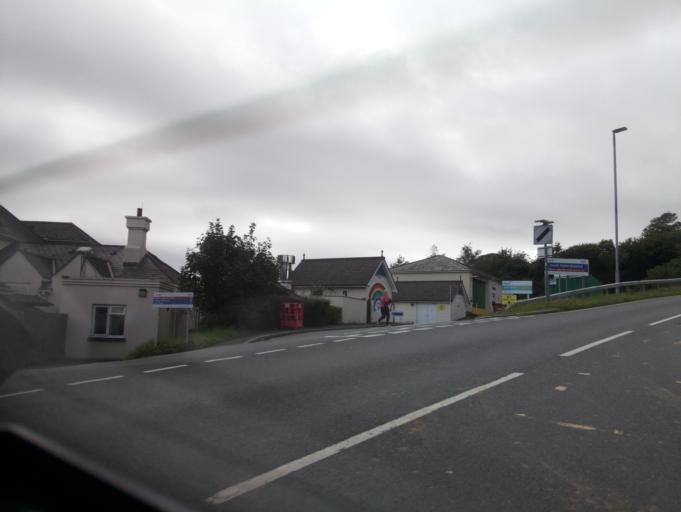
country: GB
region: England
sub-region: Devon
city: Kingsbridge
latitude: 50.2894
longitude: -3.7812
